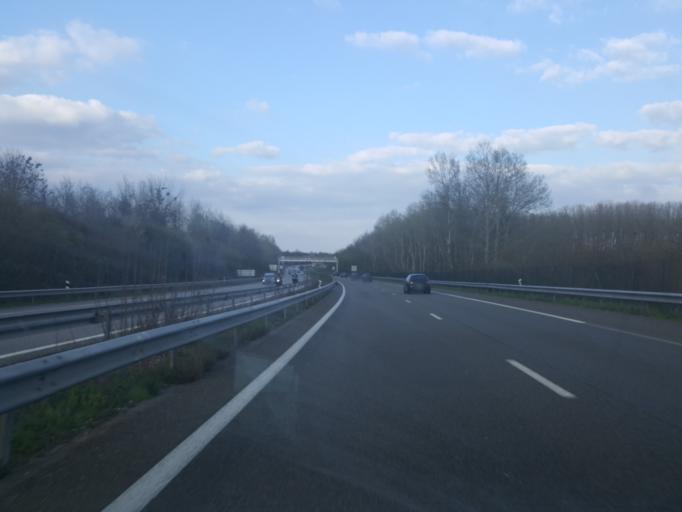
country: FR
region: Ile-de-France
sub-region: Departement des Yvelines
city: Houdan
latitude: 48.7855
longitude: 1.6230
